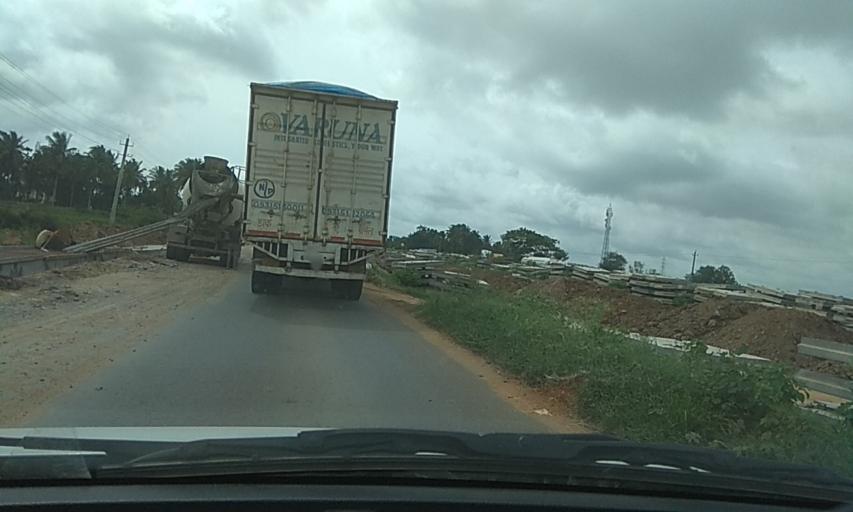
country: IN
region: Karnataka
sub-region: Davanagere
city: Mayakonda
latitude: 14.4243
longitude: 75.9756
